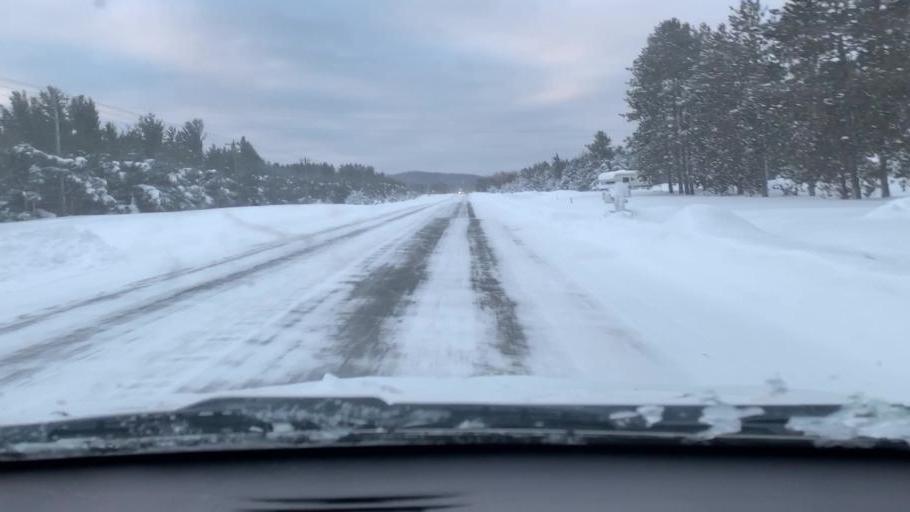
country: US
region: Michigan
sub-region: Antrim County
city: Mancelona
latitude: 44.9218
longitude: -85.0510
